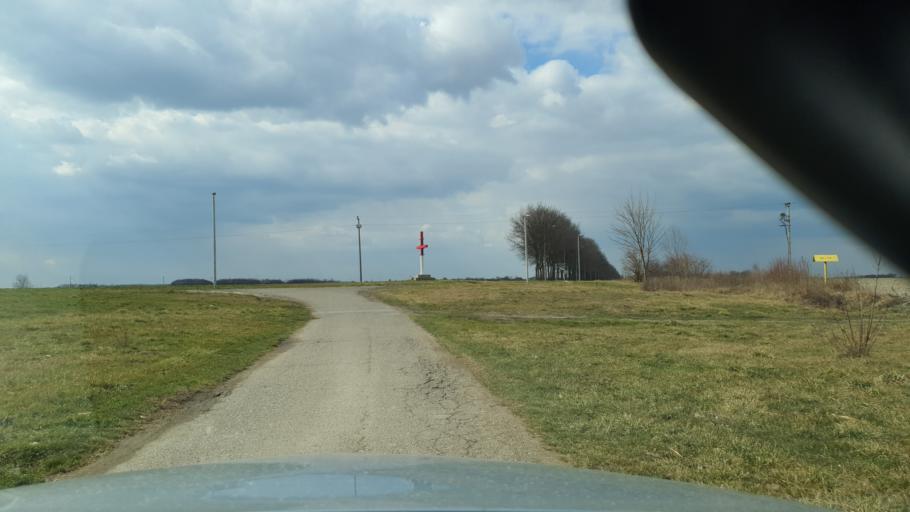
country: RS
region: Autonomna Pokrajina Vojvodina
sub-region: Juznobacki Okrug
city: Bac
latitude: 45.3923
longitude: 19.2198
